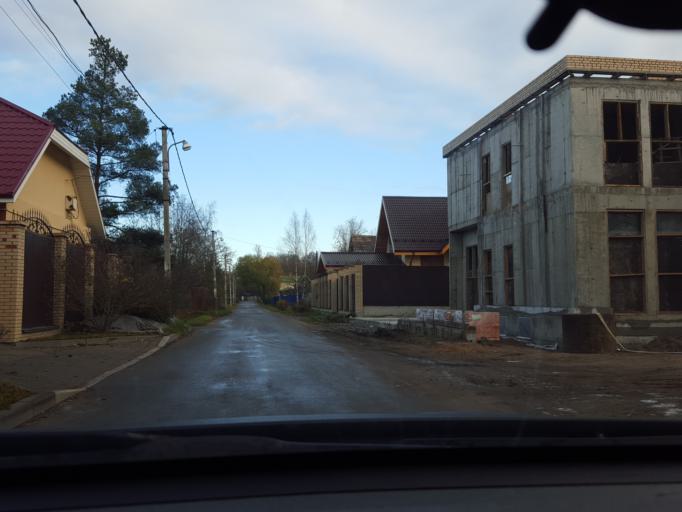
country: RU
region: St.-Petersburg
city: Shuvalovo
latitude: 60.0407
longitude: 30.2951
